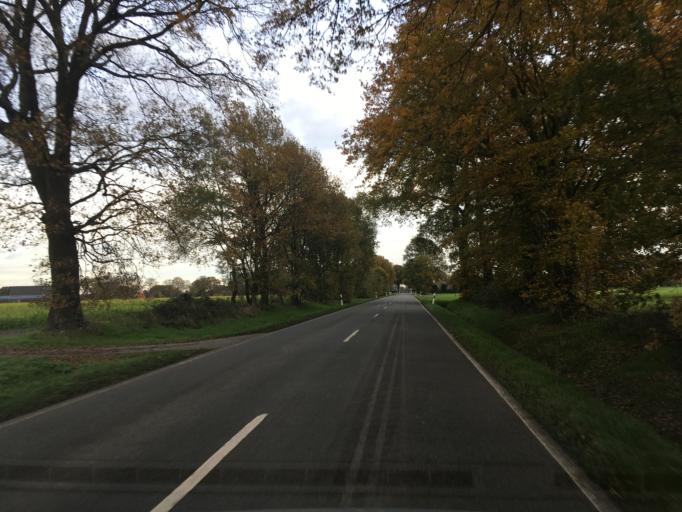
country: DE
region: North Rhine-Westphalia
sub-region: Regierungsbezirk Munster
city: Raesfeld
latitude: 51.7401
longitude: 6.8385
